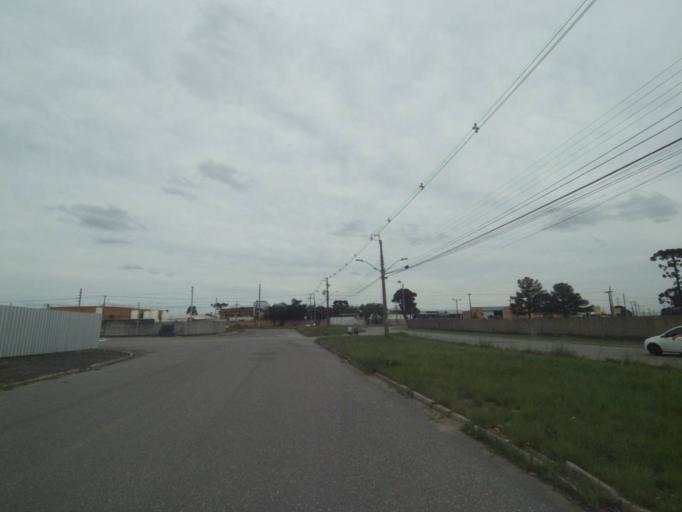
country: BR
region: Parana
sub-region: Curitiba
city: Curitiba
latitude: -25.5197
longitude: -49.3301
